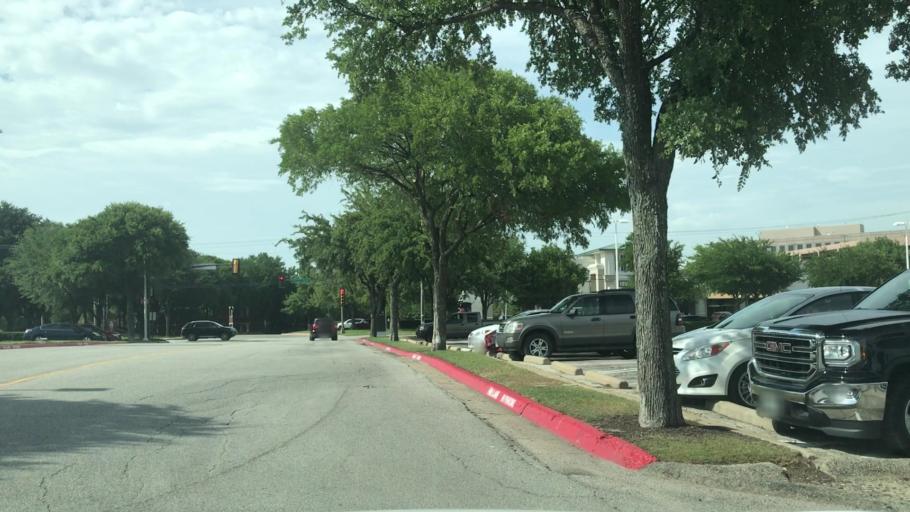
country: US
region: Texas
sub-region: Dallas County
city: University Park
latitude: 32.8711
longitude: -96.7732
